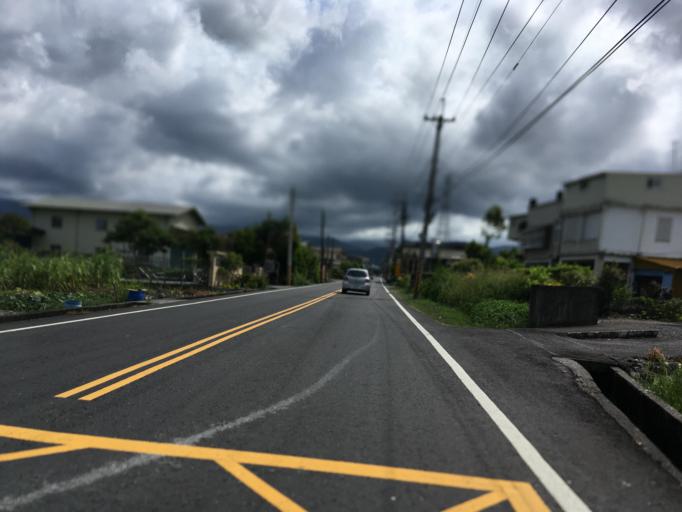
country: TW
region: Taiwan
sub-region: Yilan
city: Yilan
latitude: 24.6681
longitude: 121.7465
